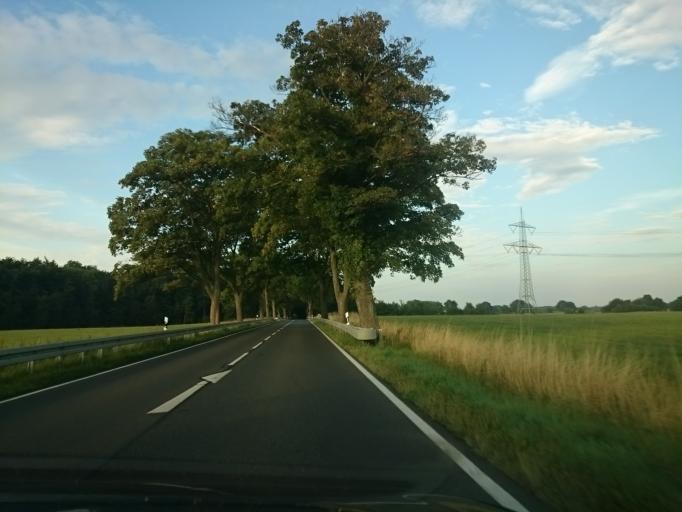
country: DE
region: Mecklenburg-Vorpommern
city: Zussow
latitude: 53.9636
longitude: 13.5247
